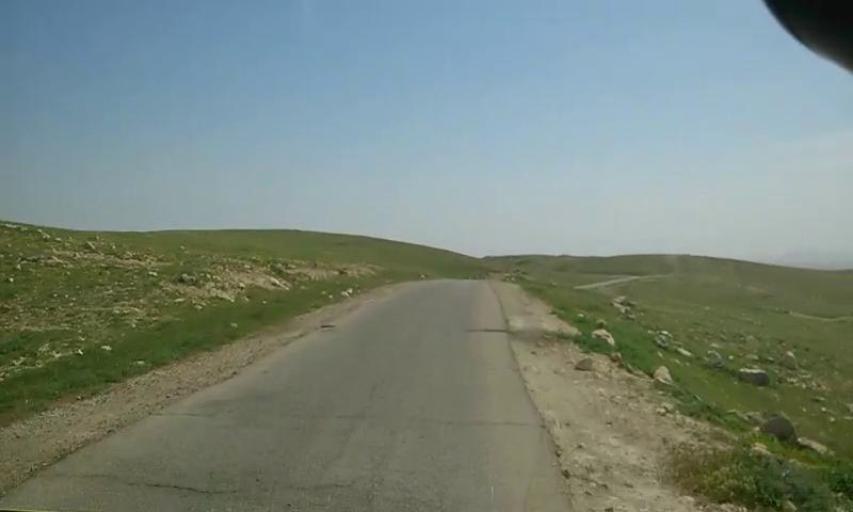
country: PS
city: `Arab ar Rashaydah
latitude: 31.5455
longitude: 35.2583
